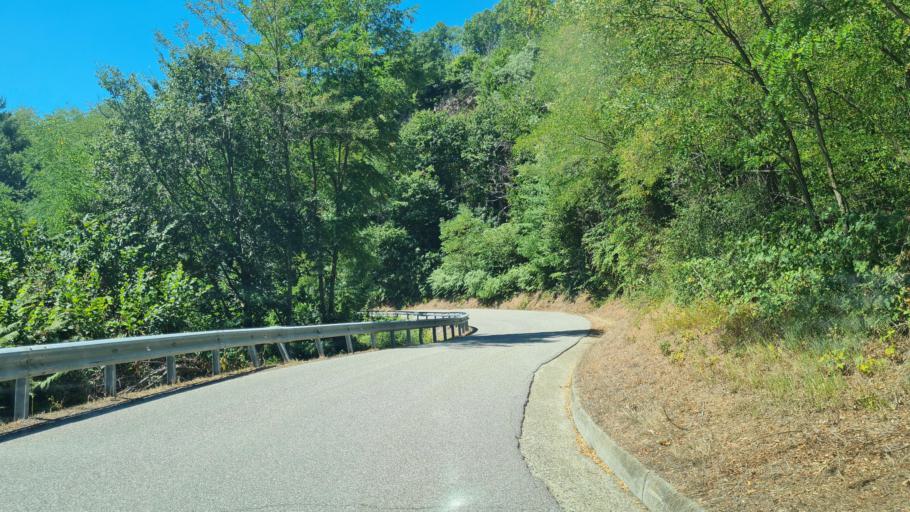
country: IT
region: Piedmont
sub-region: Provincia di Biella
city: Masserano
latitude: 45.6007
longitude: 8.2070
